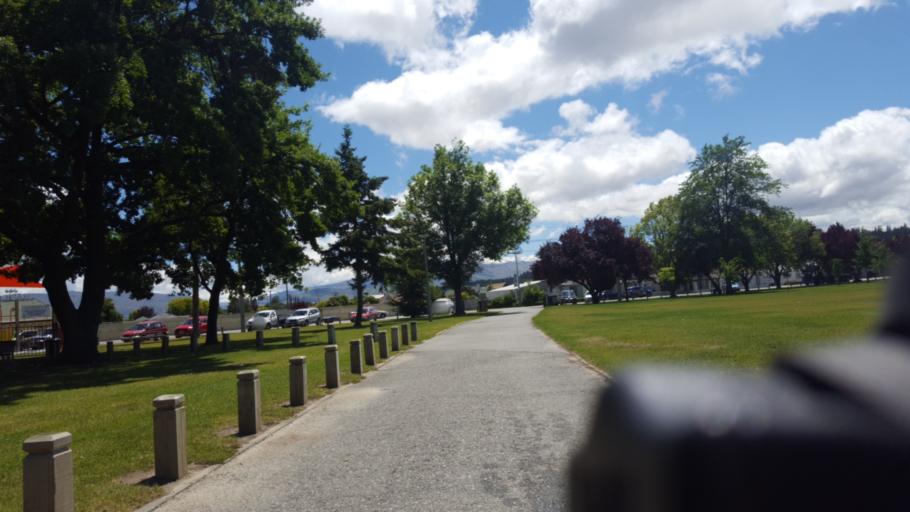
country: NZ
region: Otago
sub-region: Queenstown-Lakes District
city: Wanaka
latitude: -45.2535
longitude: 169.3917
